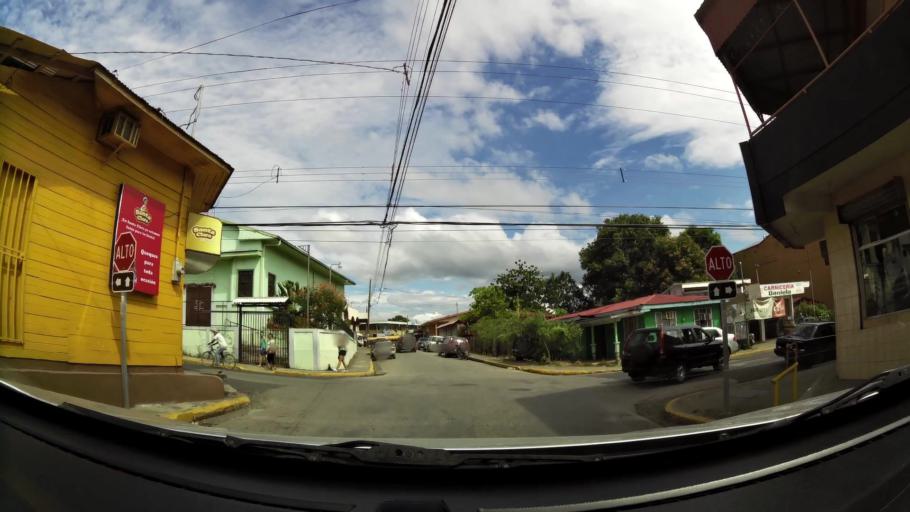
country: CR
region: Guanacaste
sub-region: Canton de Nicoya
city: Nicoya
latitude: 10.1417
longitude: -85.4519
